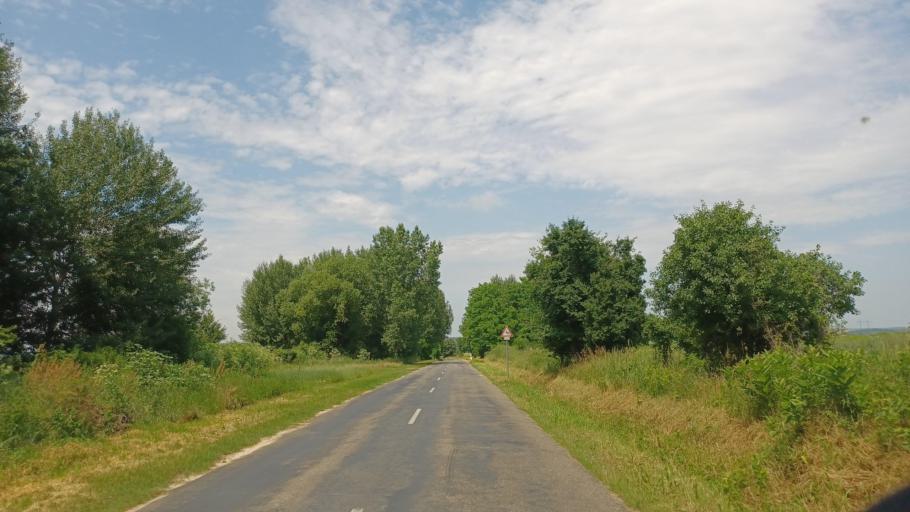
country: HU
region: Tolna
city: Simontornya
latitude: 46.7220
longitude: 18.4964
